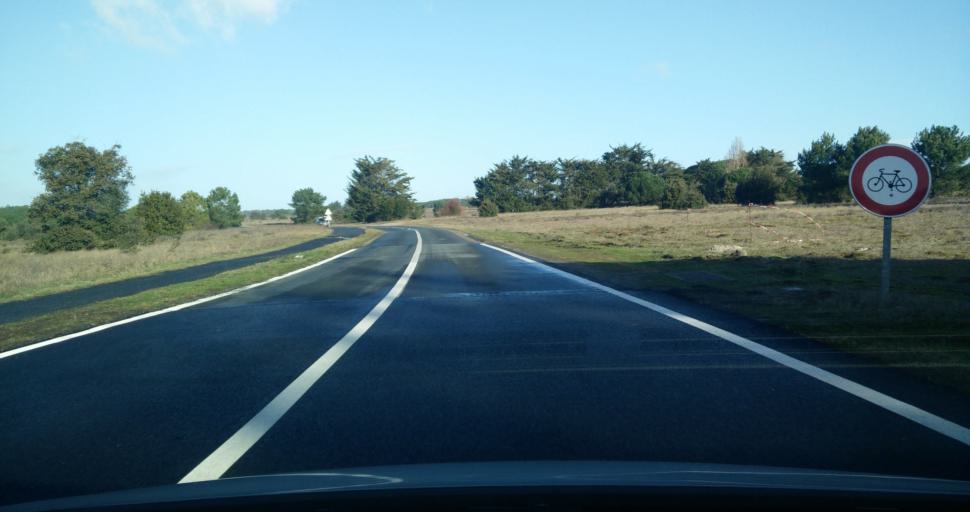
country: FR
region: Poitou-Charentes
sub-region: Departement de la Charente-Maritime
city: Sainte-Marie-de-Re
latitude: 46.1557
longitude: -1.3150
